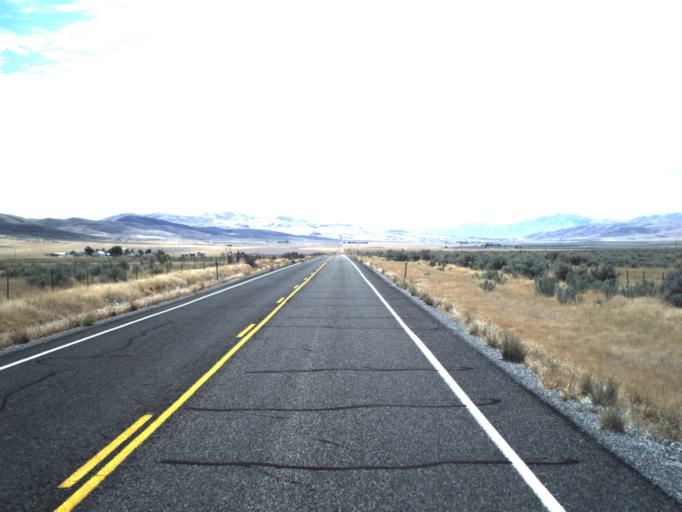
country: US
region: Utah
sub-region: Box Elder County
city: Garland
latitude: 41.8029
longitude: -112.4164
